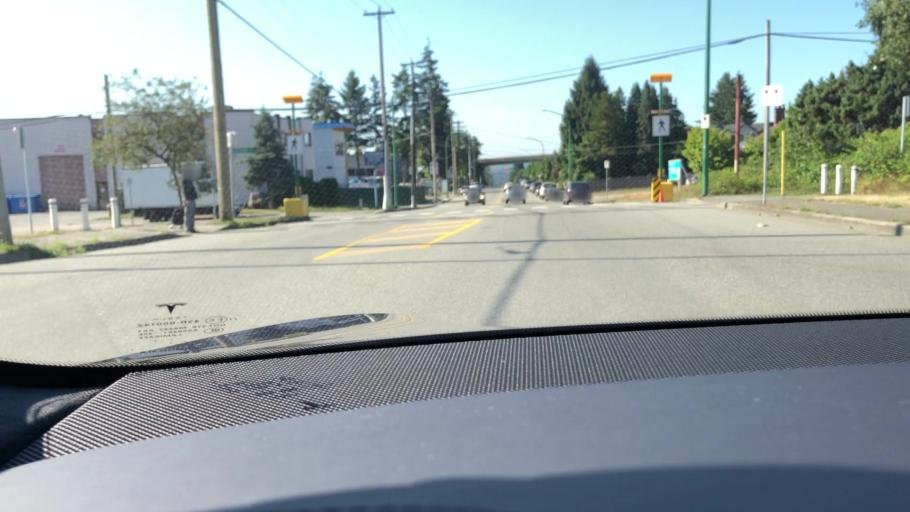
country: CA
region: British Columbia
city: Burnaby
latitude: 49.2175
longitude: -122.9721
